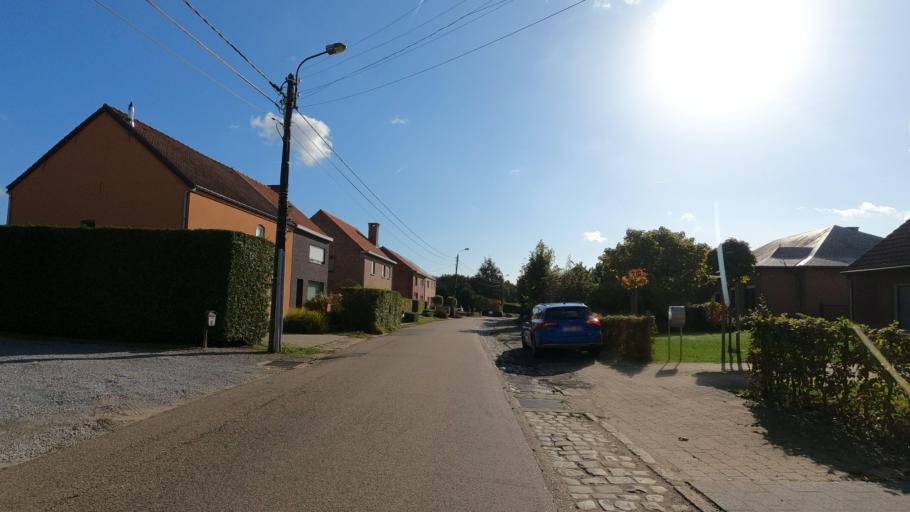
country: BE
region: Flanders
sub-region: Provincie Vlaams-Brabant
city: Aarschot
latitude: 50.9759
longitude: 4.8422
